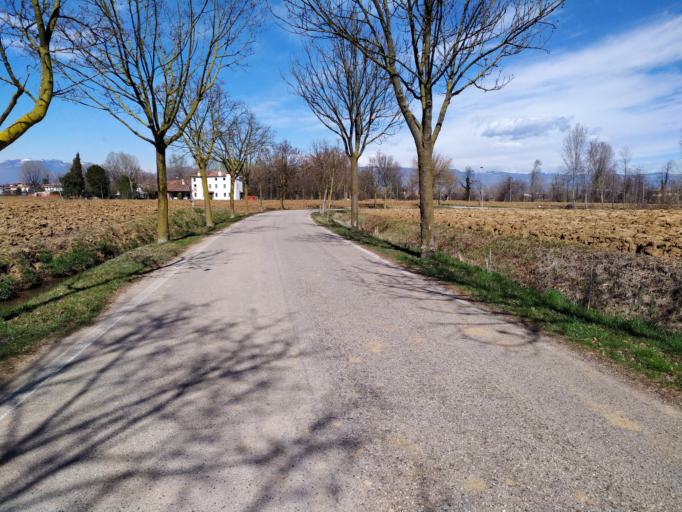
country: IT
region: Veneto
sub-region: Provincia di Vicenza
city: Motta
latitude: 45.5963
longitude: 11.5048
